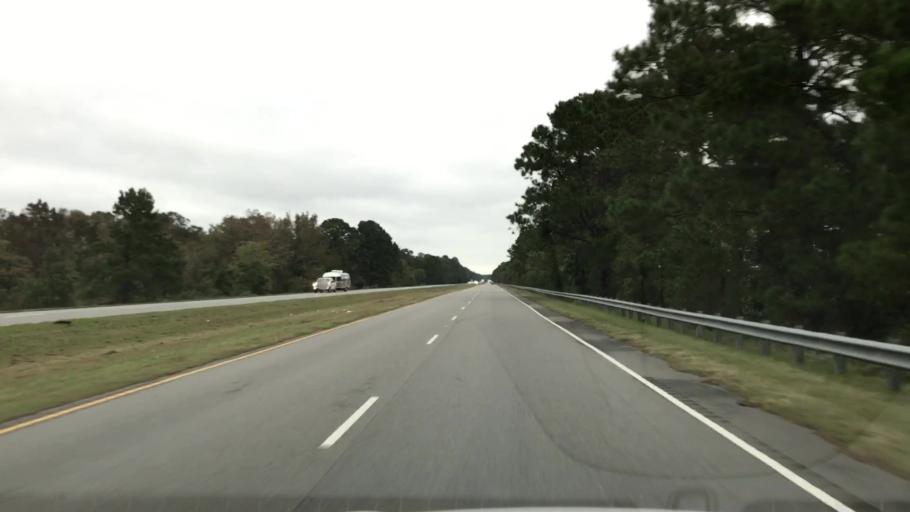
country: US
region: South Carolina
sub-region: Georgetown County
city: Georgetown
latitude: 33.1914
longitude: -79.3993
